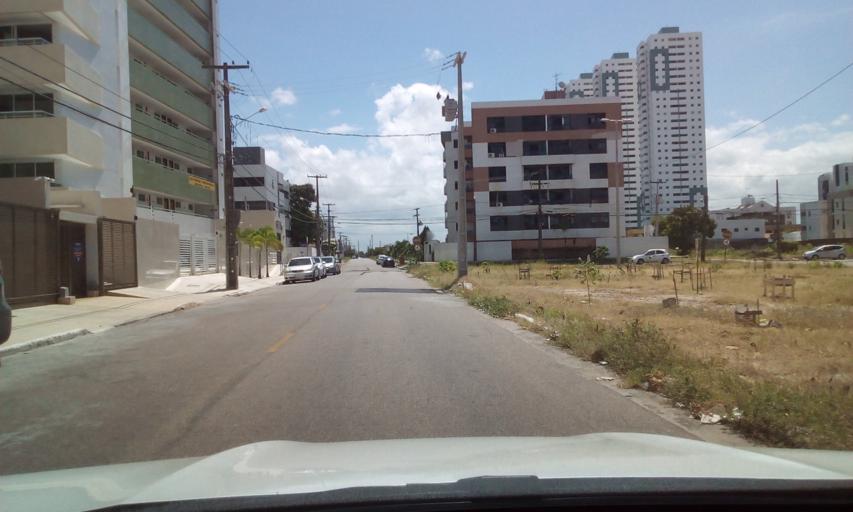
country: BR
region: Paraiba
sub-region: Joao Pessoa
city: Joao Pessoa
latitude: -7.0730
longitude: -34.8378
